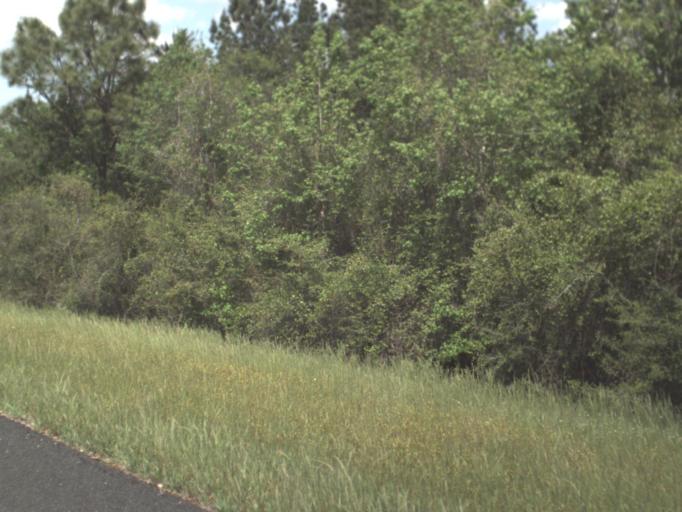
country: US
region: Florida
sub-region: Escambia County
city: Molino
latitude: 30.8120
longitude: -87.3353
